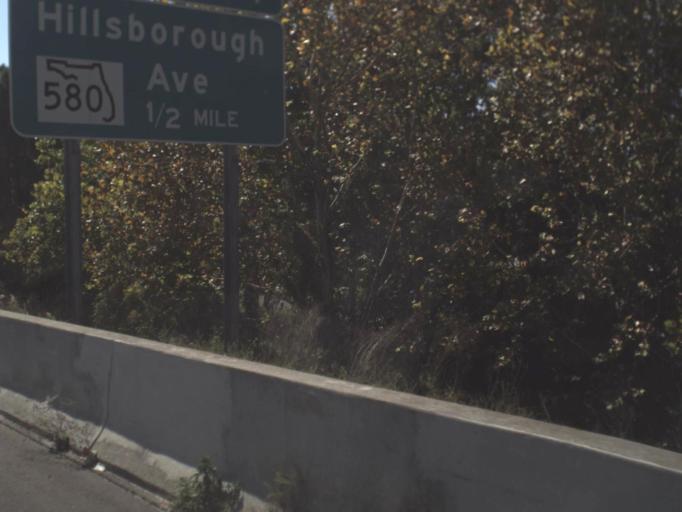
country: US
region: Florida
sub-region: Hillsborough County
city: Town 'n' Country
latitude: 28.0060
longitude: -82.5457
